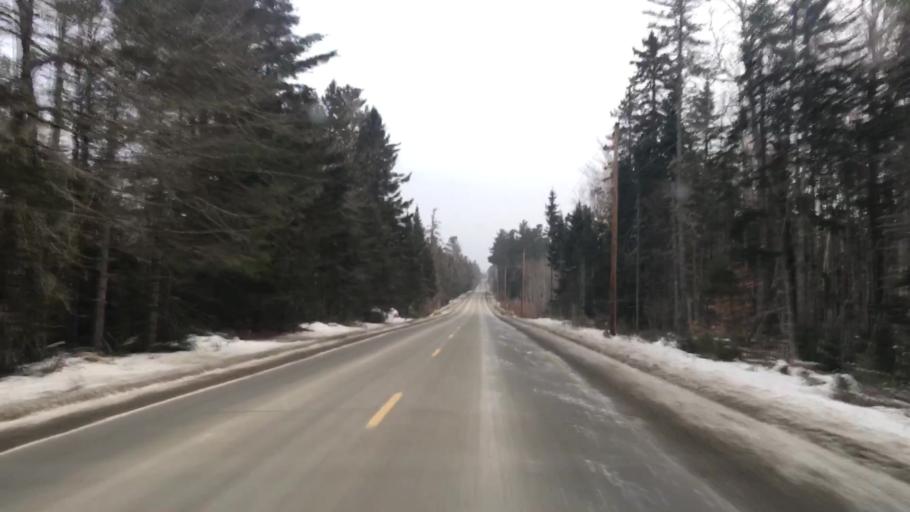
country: US
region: Maine
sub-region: Hancock County
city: Ellsworth
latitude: 44.6705
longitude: -68.3545
